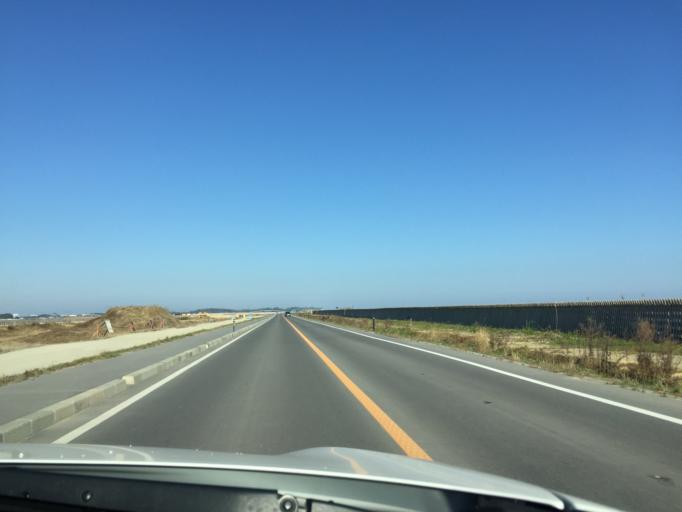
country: JP
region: Miyagi
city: Marumori
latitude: 37.7855
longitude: 140.9841
